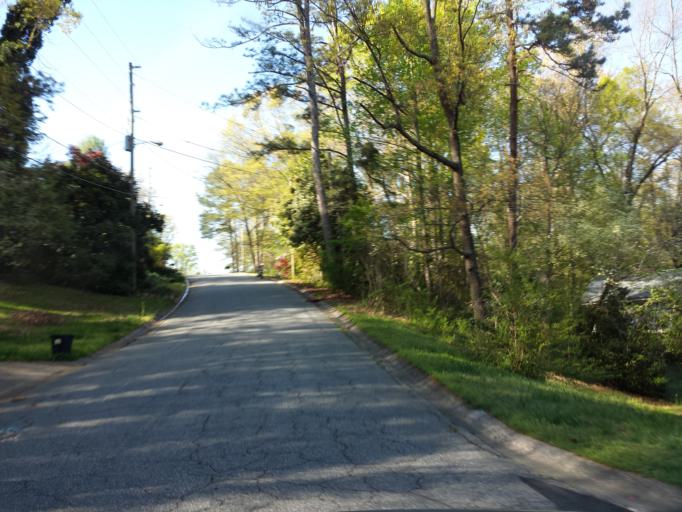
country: US
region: Georgia
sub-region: Cobb County
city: Marietta
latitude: 33.9658
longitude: -84.5207
